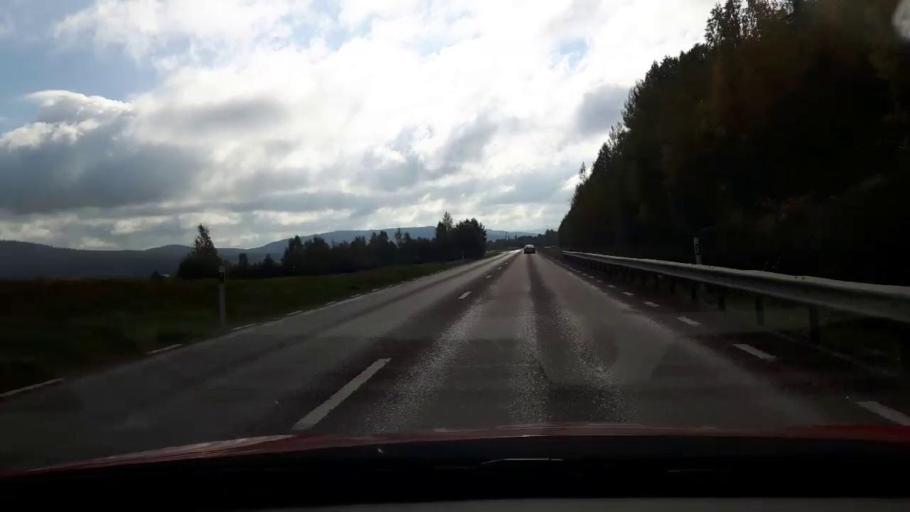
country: SE
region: Gaevleborg
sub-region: Ljusdals Kommun
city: Jaervsoe
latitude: 61.7313
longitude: 16.1651
